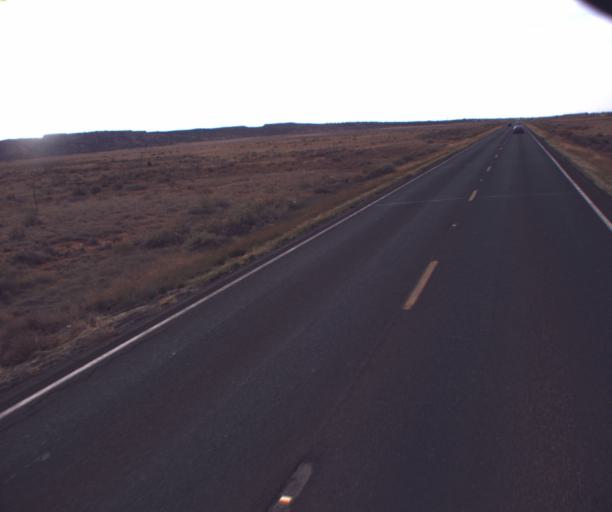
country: US
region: Arizona
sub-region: Apache County
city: Ganado
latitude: 35.7847
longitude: -109.6183
